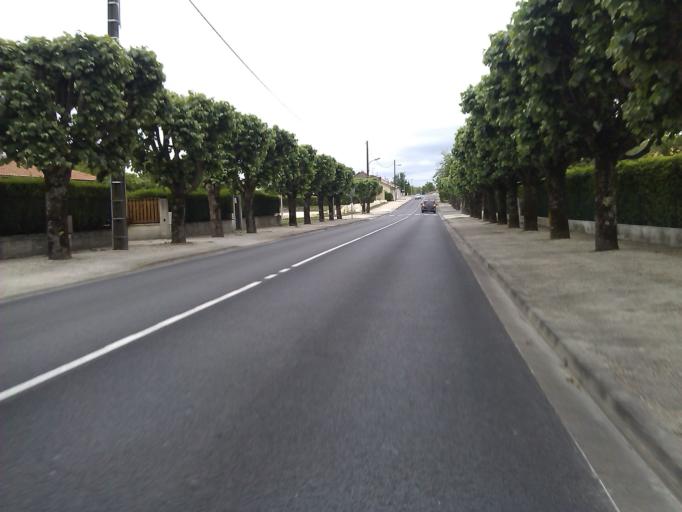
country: FR
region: Poitou-Charentes
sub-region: Departement de la Charente
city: Barbezieux-Saint-Hilaire
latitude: 45.4780
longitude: -0.1508
